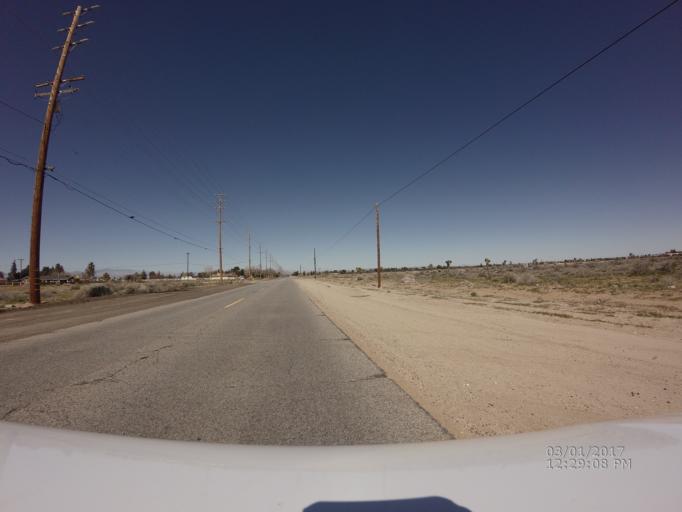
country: US
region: California
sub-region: Los Angeles County
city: Desert View Highlands
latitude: 34.6377
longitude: -118.1656
